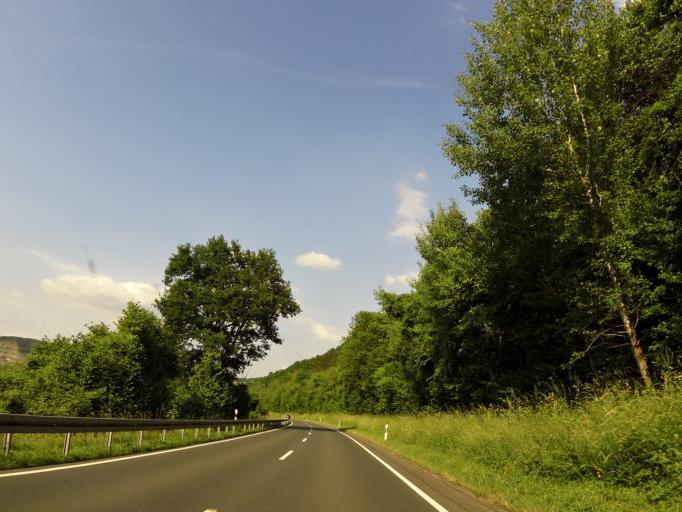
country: DE
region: Bavaria
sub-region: Regierungsbezirk Unterfranken
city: Marktheidenfeld
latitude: 49.7866
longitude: 9.6088
